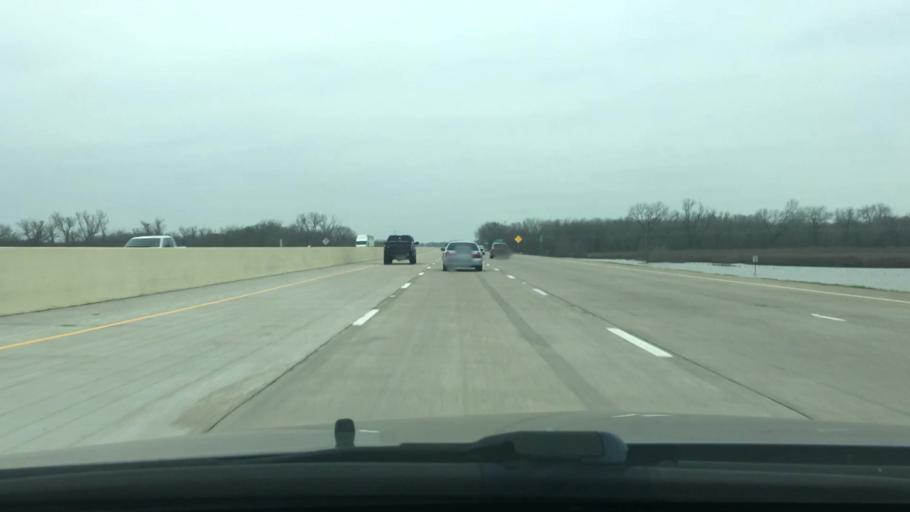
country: US
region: Texas
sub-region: Navarro County
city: Corsicana
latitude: 31.9537
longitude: -96.4211
